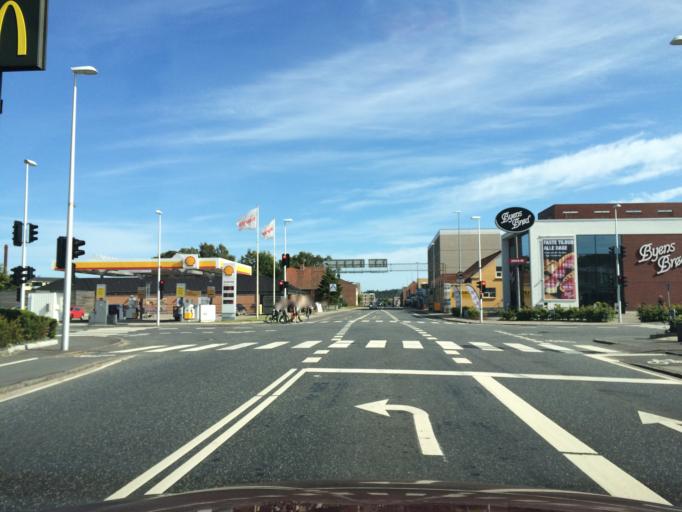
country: DK
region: Central Jutland
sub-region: Silkeborg Kommune
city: Silkeborg
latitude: 56.1843
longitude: 9.5446
